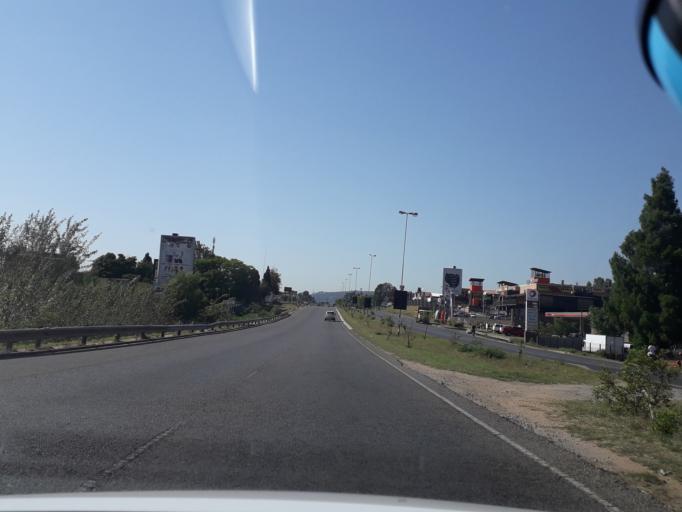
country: ZA
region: Gauteng
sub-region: City of Johannesburg Metropolitan Municipality
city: Roodepoort
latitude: -26.0890
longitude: 27.9368
